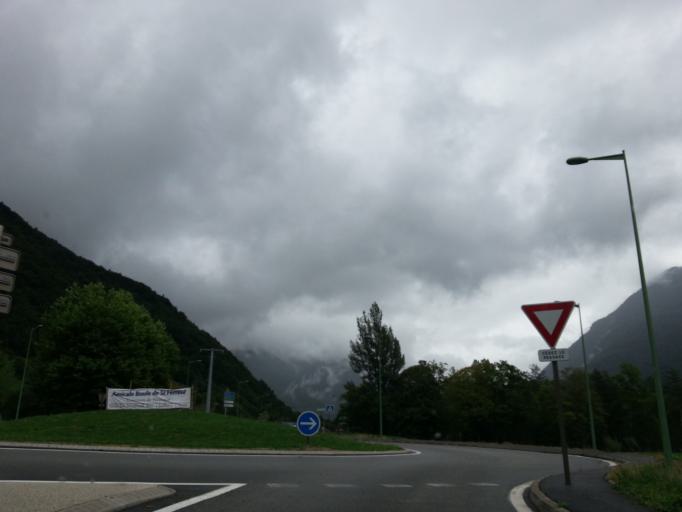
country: FR
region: Rhone-Alpes
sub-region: Departement de la Haute-Savoie
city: Faverges
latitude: 45.7591
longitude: 6.3176
